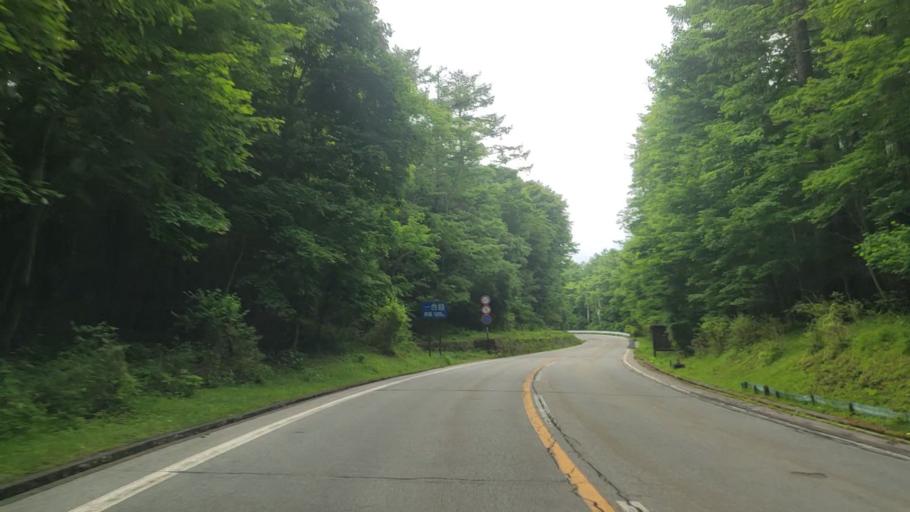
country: JP
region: Yamanashi
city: Fujikawaguchiko
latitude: 35.4176
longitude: 138.7383
